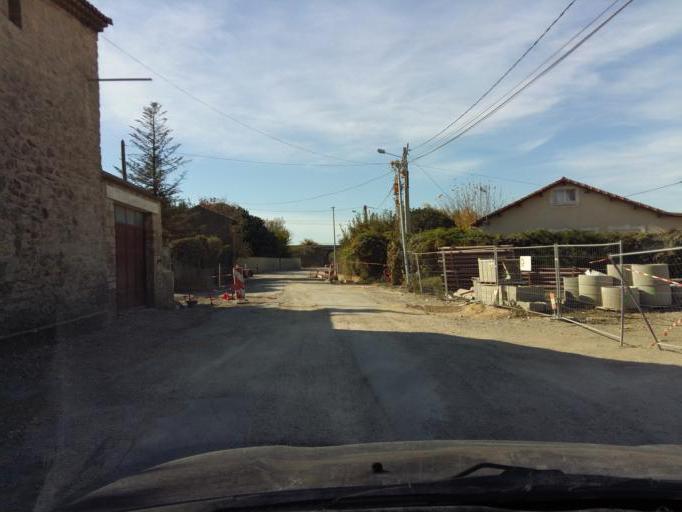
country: FR
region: Provence-Alpes-Cote d'Azur
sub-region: Departement du Vaucluse
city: Piolenc
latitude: 44.1794
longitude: 4.7689
